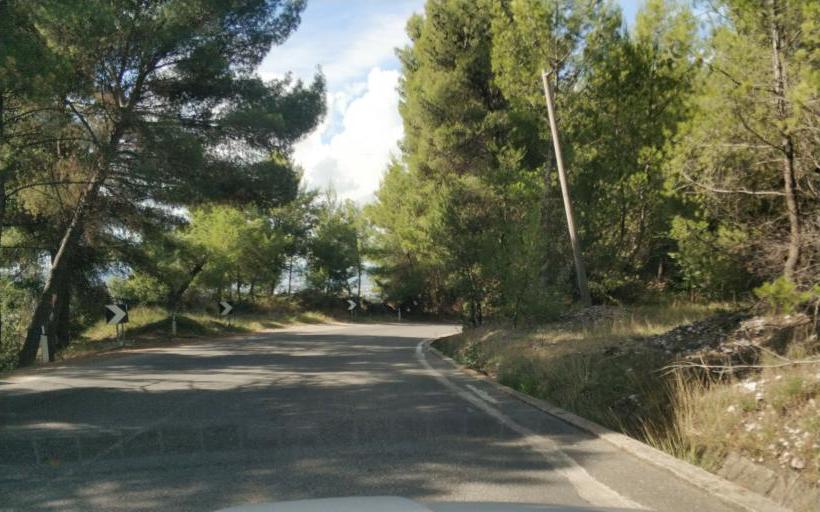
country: AL
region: Durres
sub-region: Rrethi i Krujes
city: Kruje
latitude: 41.4884
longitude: 19.7671
